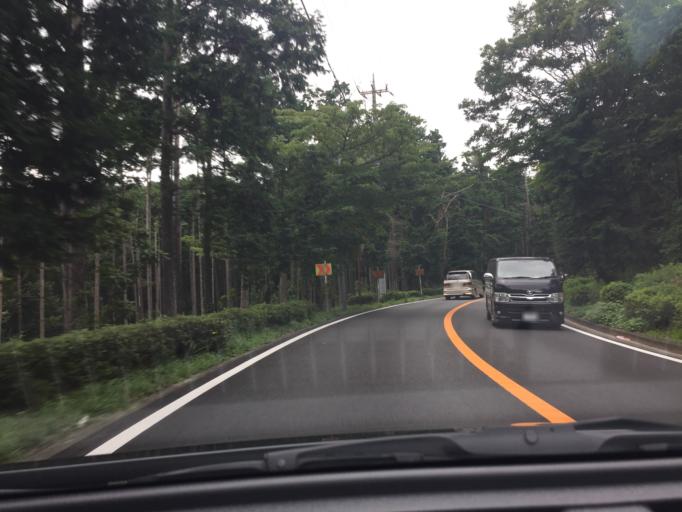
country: JP
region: Shizuoka
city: Ito
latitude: 34.9229
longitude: 139.1263
